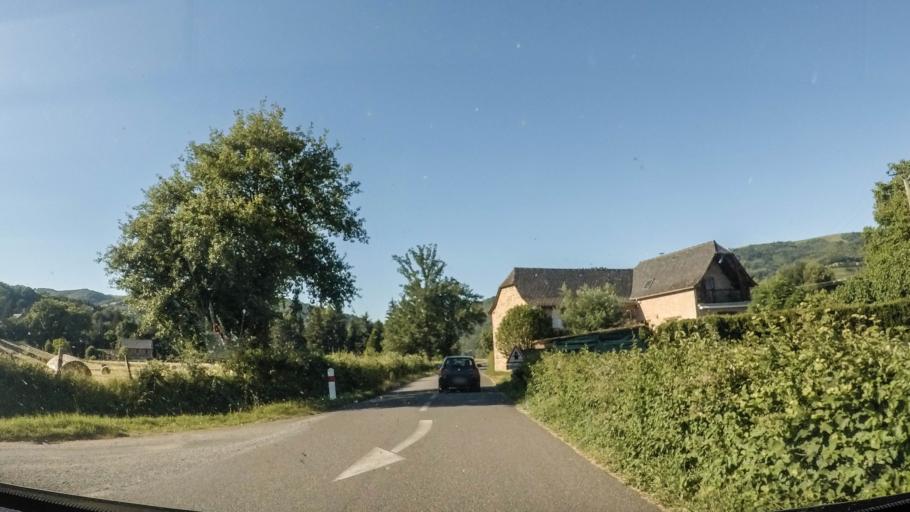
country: FR
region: Midi-Pyrenees
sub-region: Departement de l'Aveyron
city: Saint-Christophe-Vallon
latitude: 44.5477
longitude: 2.4045
